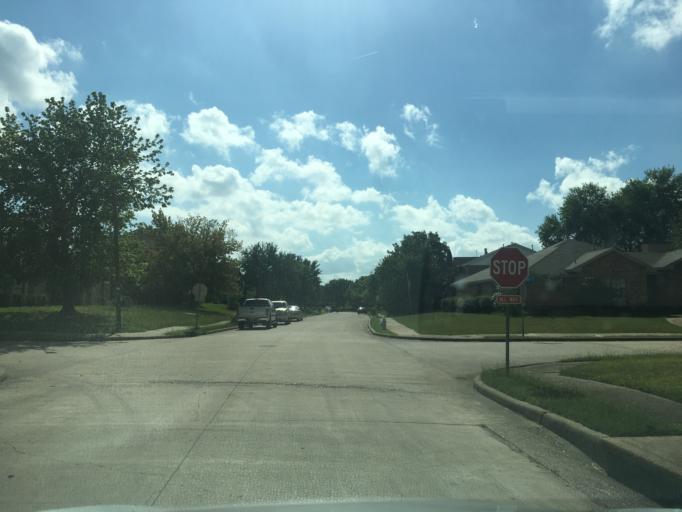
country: US
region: Texas
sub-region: Dallas County
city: Sachse
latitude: 32.9682
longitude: -96.5982
